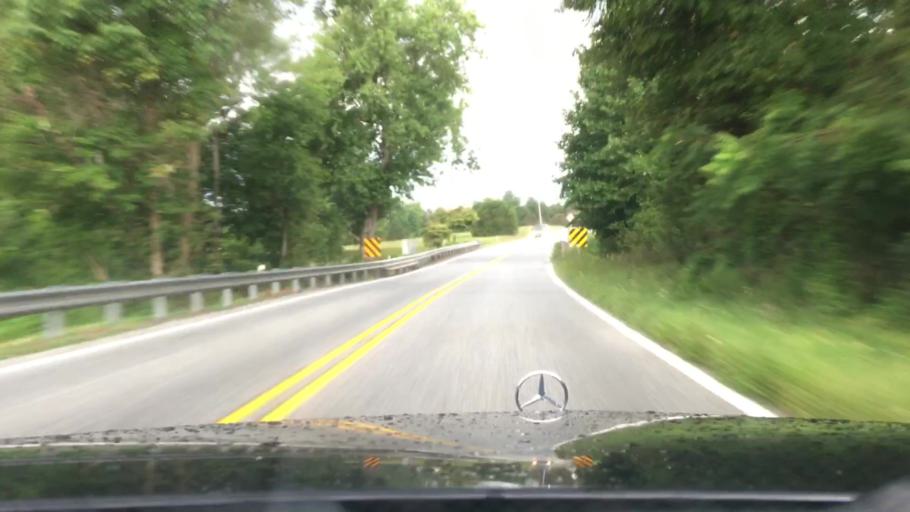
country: US
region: Virginia
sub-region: Nelson County
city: Lovingston
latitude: 37.7585
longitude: -78.9802
